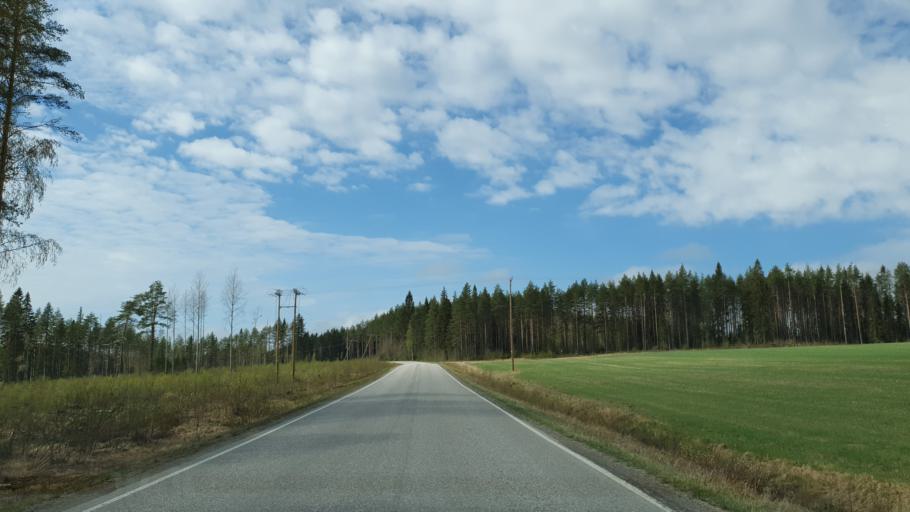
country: FI
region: Kainuu
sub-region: Kehys-Kainuu
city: Kuhmo
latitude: 64.1204
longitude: 29.6889
